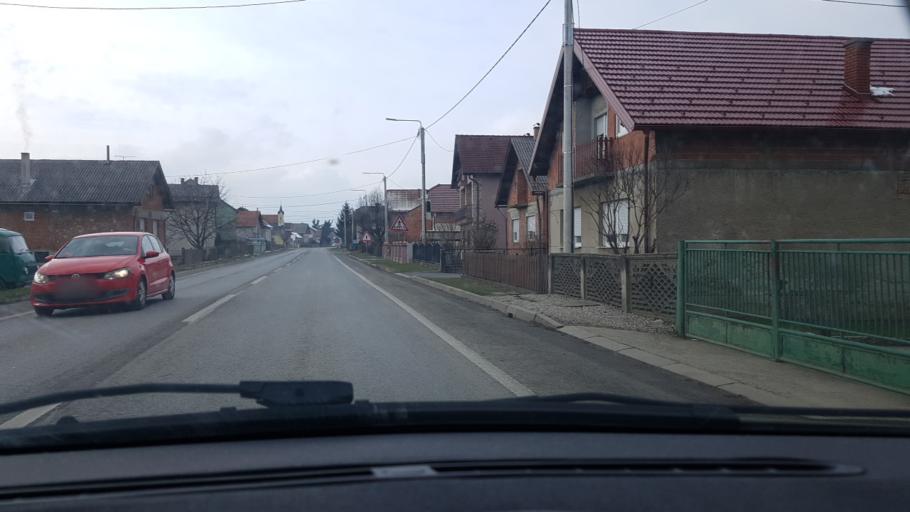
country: HR
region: Varazdinska
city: Nedeljanec
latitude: 46.2860
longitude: 16.2707
